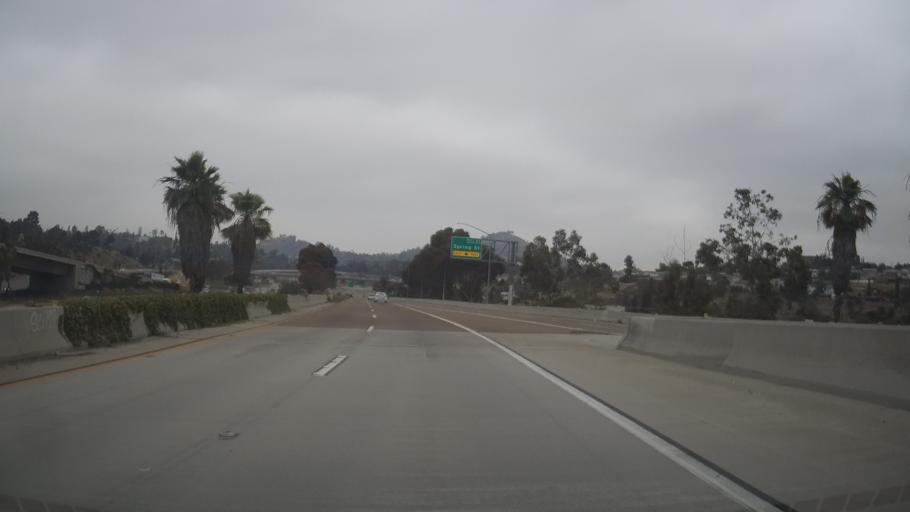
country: US
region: California
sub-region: San Diego County
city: Lemon Grove
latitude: 32.7478
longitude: -117.0173
